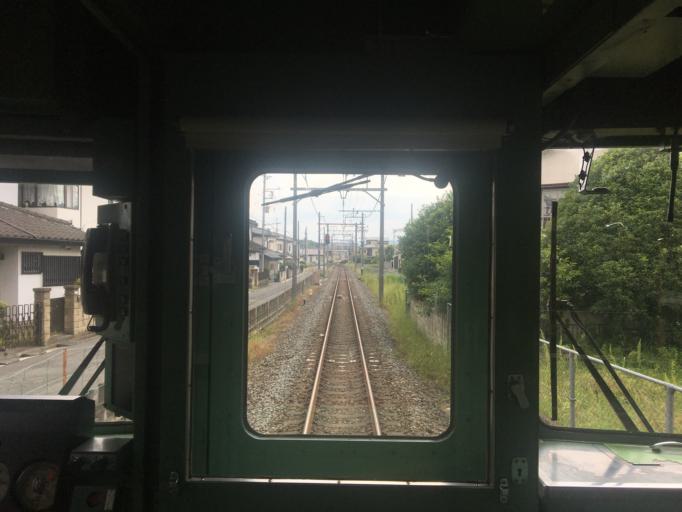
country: JP
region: Saitama
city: Sakado
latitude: 35.9418
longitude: 139.3722
